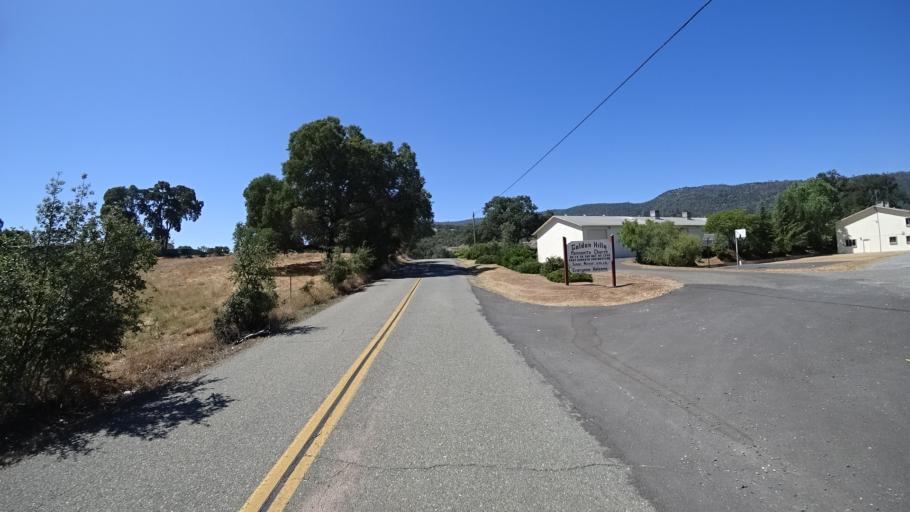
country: US
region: California
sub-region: Calaveras County
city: San Andreas
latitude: 38.1817
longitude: -120.6808
